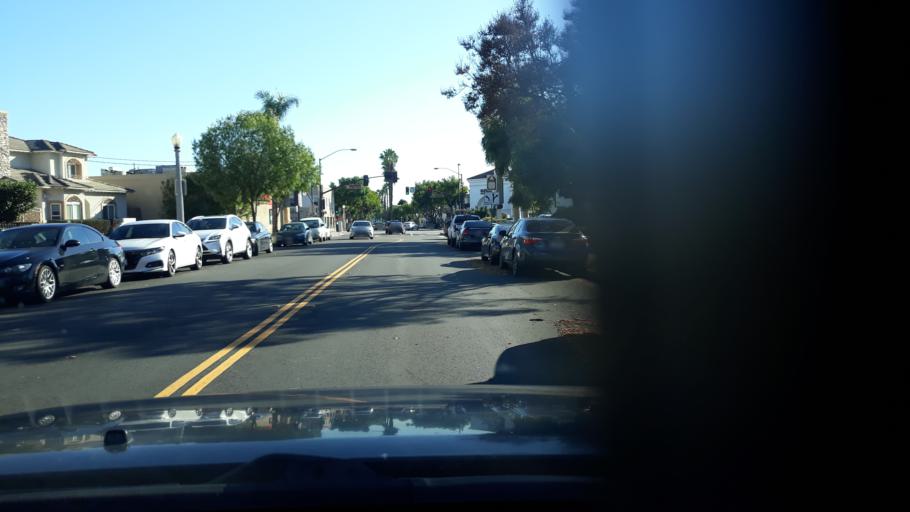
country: US
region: California
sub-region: Los Angeles County
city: San Gabriel
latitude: 34.1034
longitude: -118.1113
